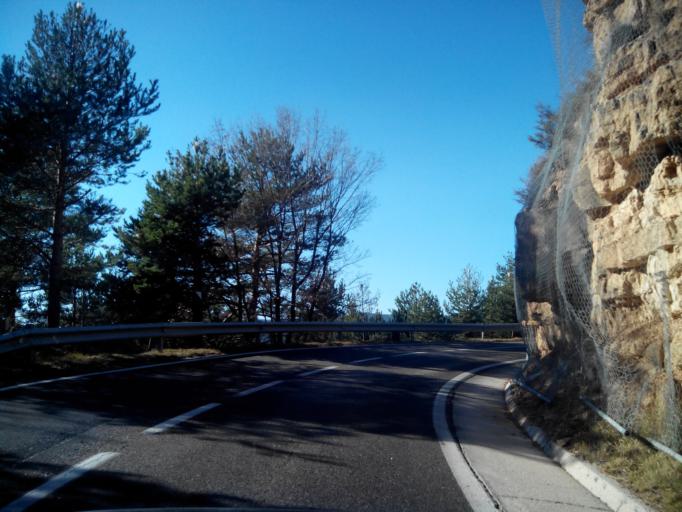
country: ES
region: Catalonia
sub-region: Provincia de Barcelona
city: Castellar del Riu
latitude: 42.0955
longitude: 1.8024
